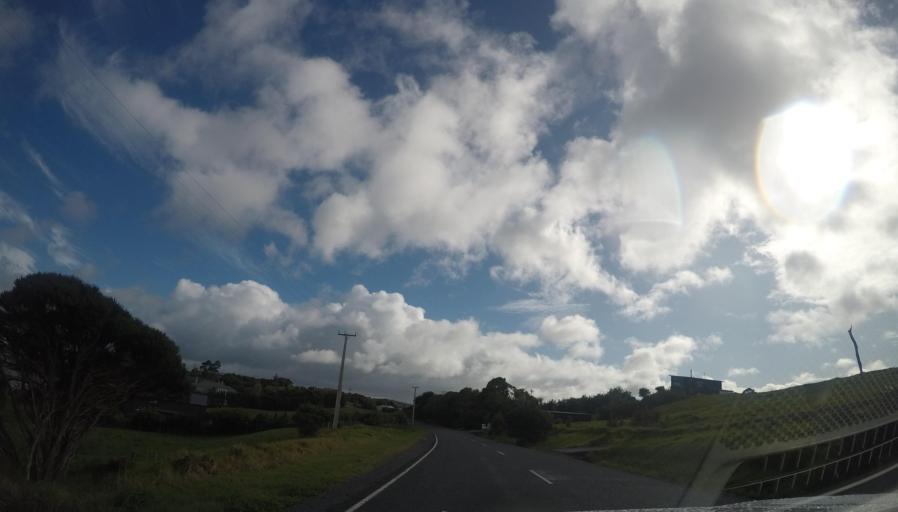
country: NZ
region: Auckland
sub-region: Auckland
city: Warkworth
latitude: -36.4679
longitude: 174.7360
